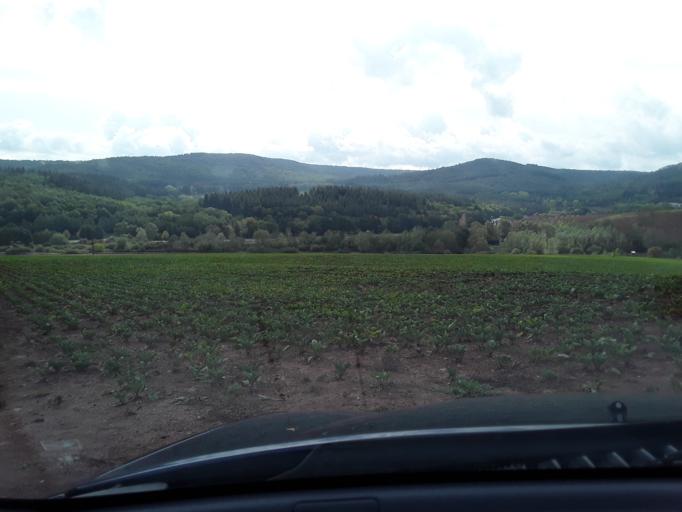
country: DE
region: Rheinland-Pfalz
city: Ramsen
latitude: 49.5489
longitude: 8.0318
